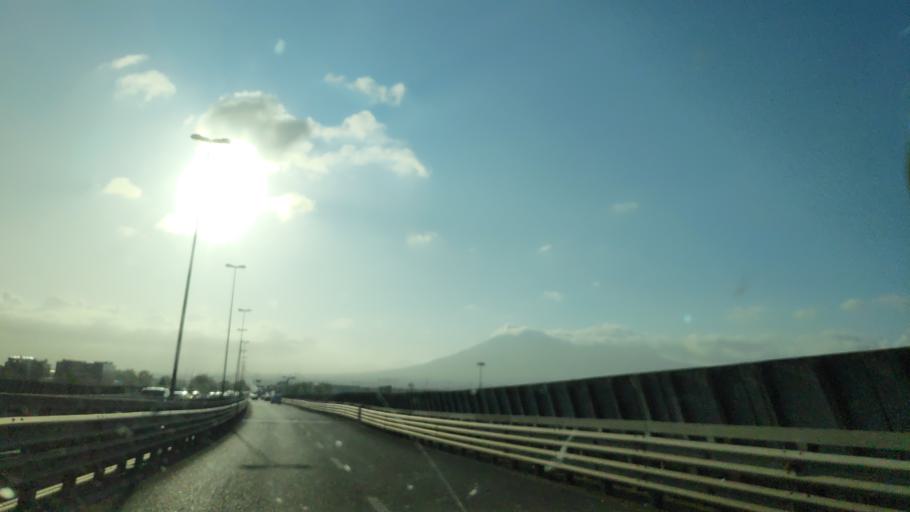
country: IT
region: Campania
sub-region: Provincia di Napoli
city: Casavatore
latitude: 40.8635
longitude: 14.2864
